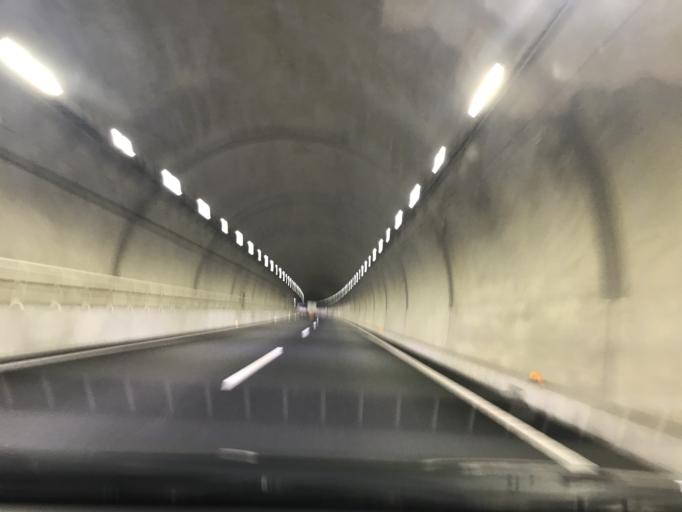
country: JP
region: Hyogo
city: Kawanishi
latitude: 34.8887
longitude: 135.3828
